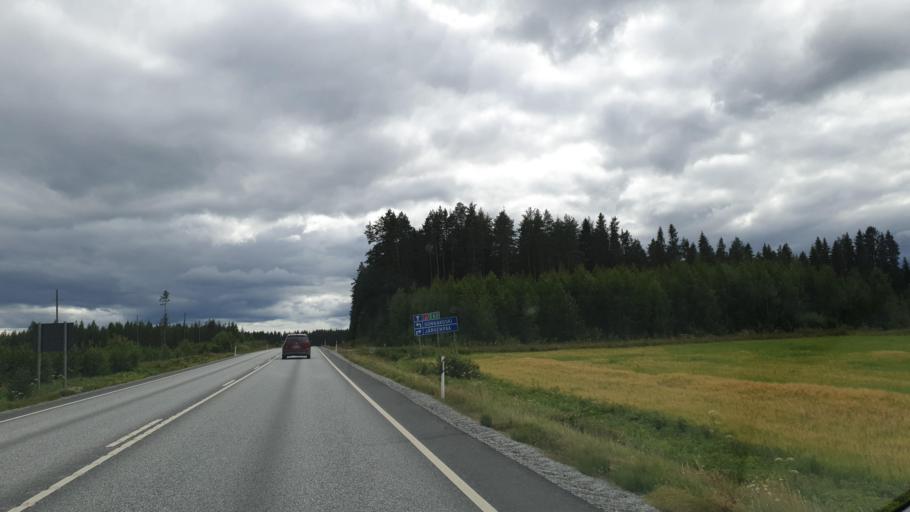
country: FI
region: Northern Savo
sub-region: Ylae-Savo
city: Sonkajaervi
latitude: 63.8536
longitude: 27.4407
